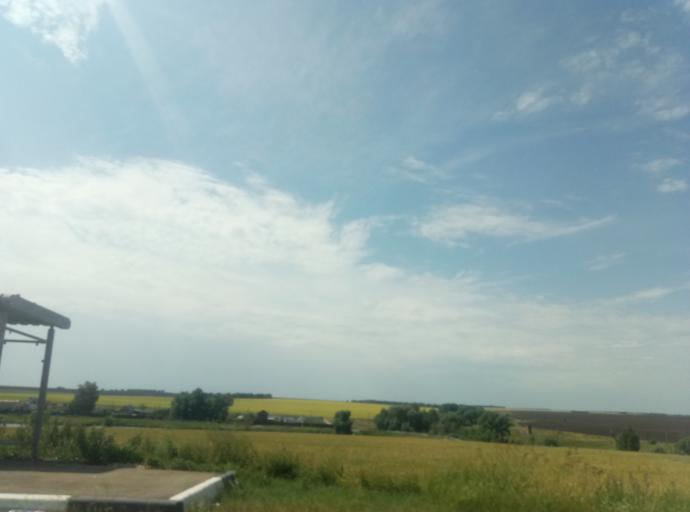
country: RU
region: Tula
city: Kireyevsk
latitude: 53.9081
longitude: 37.9721
